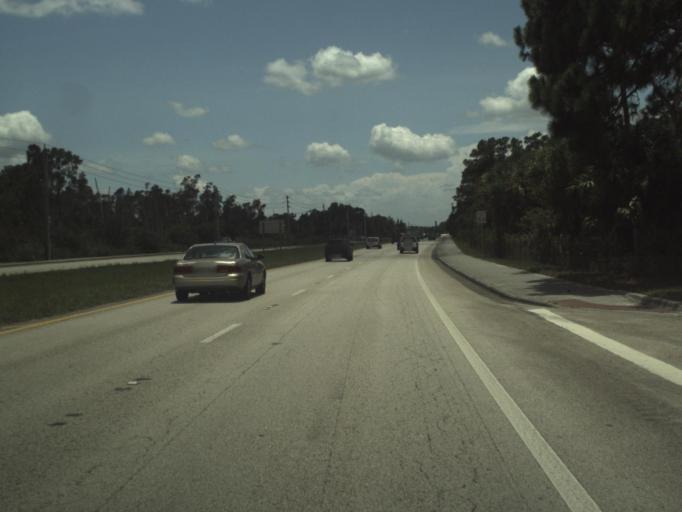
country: US
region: Florida
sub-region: Martin County
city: Palm City
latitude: 27.1447
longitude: -80.2456
